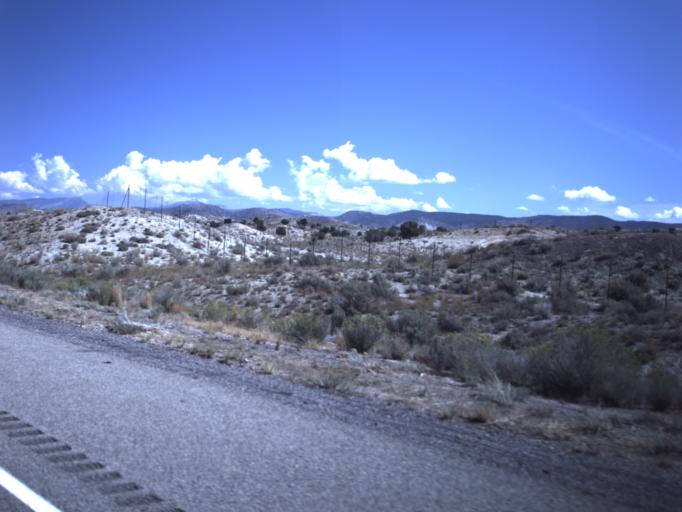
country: US
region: Utah
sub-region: Sevier County
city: Aurora
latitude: 38.8915
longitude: -111.9067
